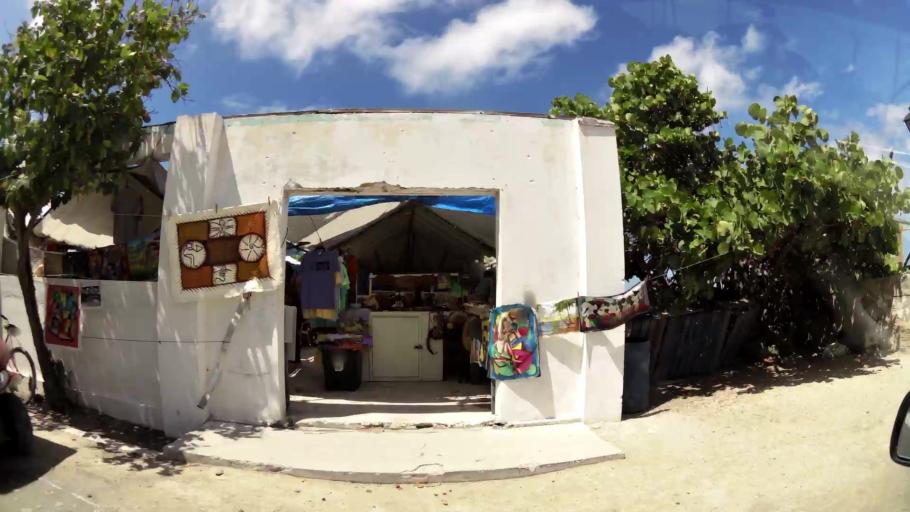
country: TC
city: Cockburn Town
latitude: 21.4729
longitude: -71.1479
